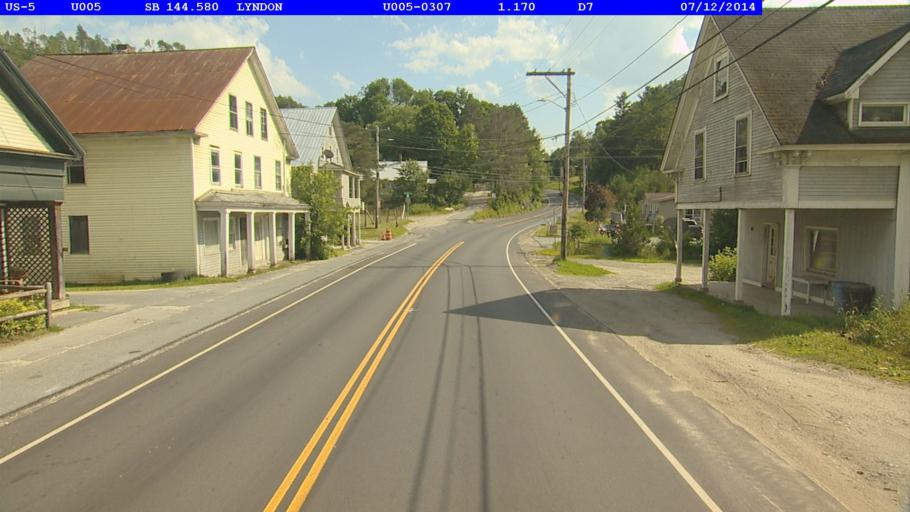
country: US
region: Vermont
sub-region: Caledonia County
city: Lyndon
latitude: 44.5136
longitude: -72.0110
